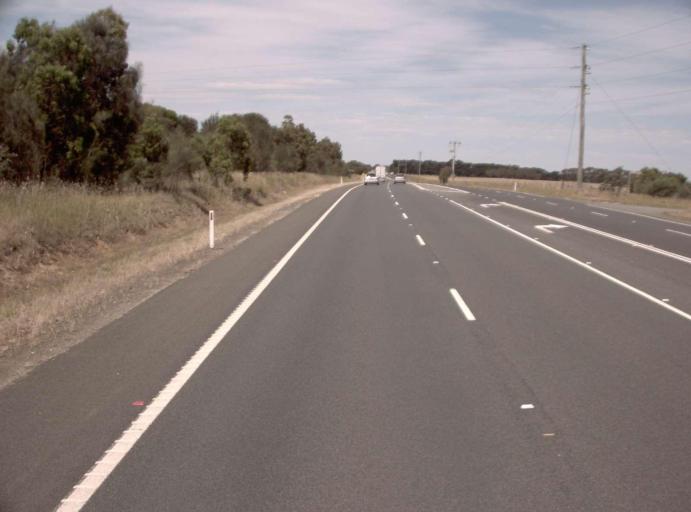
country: AU
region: Victoria
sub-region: Wellington
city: Sale
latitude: -38.1027
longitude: 146.9380
